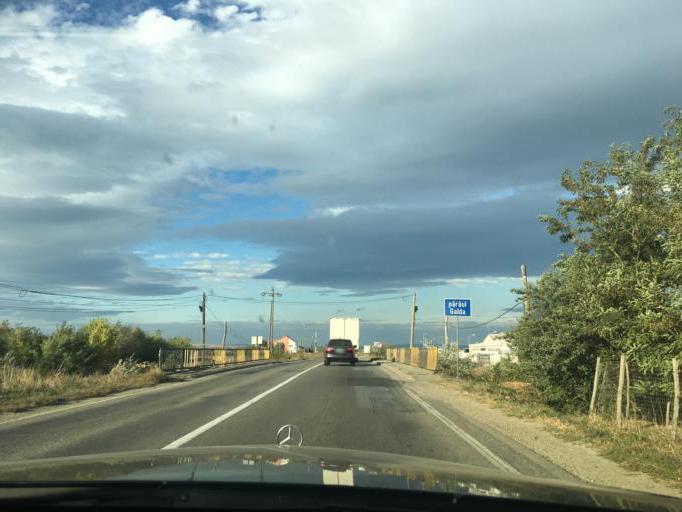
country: RO
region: Alba
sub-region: Comuna Santimbru
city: Santimbru
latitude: 46.1624
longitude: 23.6461
